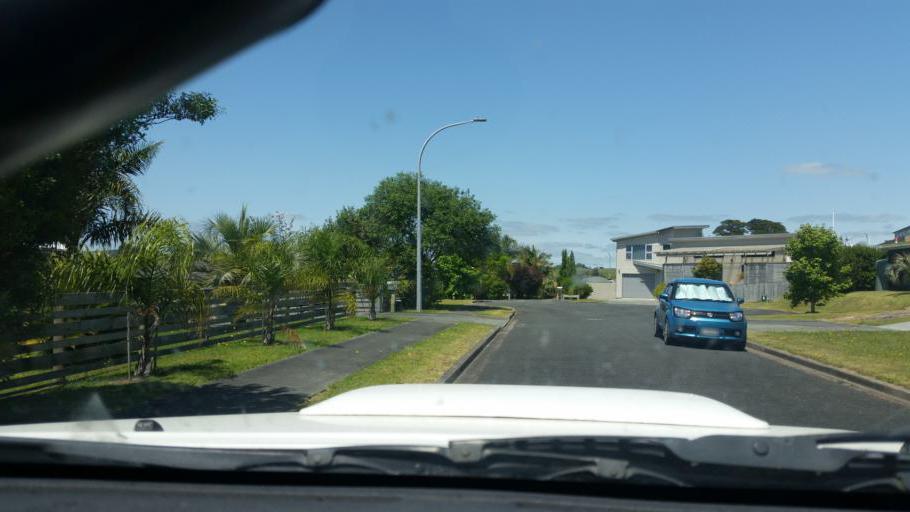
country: NZ
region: Auckland
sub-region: Auckland
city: Wellsford
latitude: -36.1248
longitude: 174.5722
